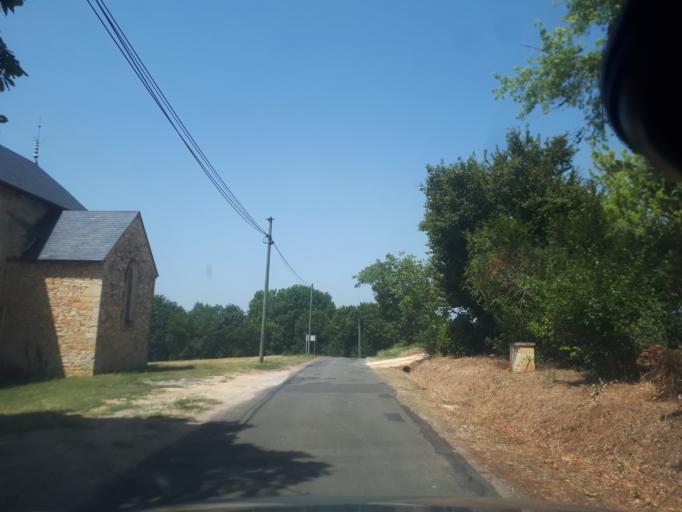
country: FR
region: Midi-Pyrenees
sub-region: Departement du Lot
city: Salviac
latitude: 44.7314
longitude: 1.2860
